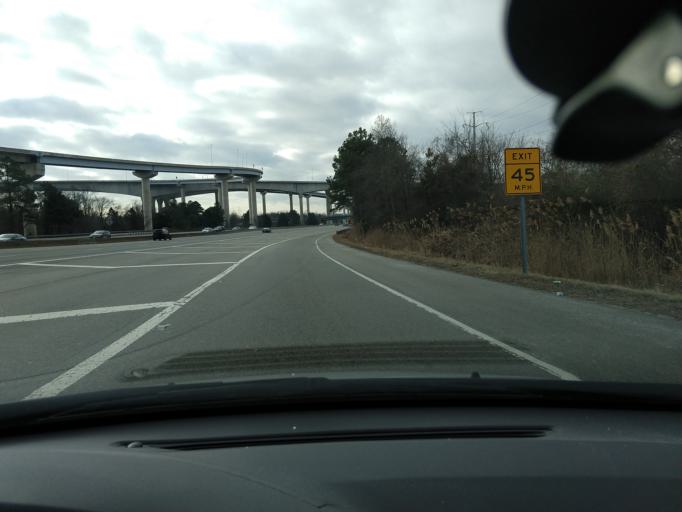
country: US
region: Virginia
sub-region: Chesterfield County
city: Bensley
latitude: 37.4465
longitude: -77.4236
